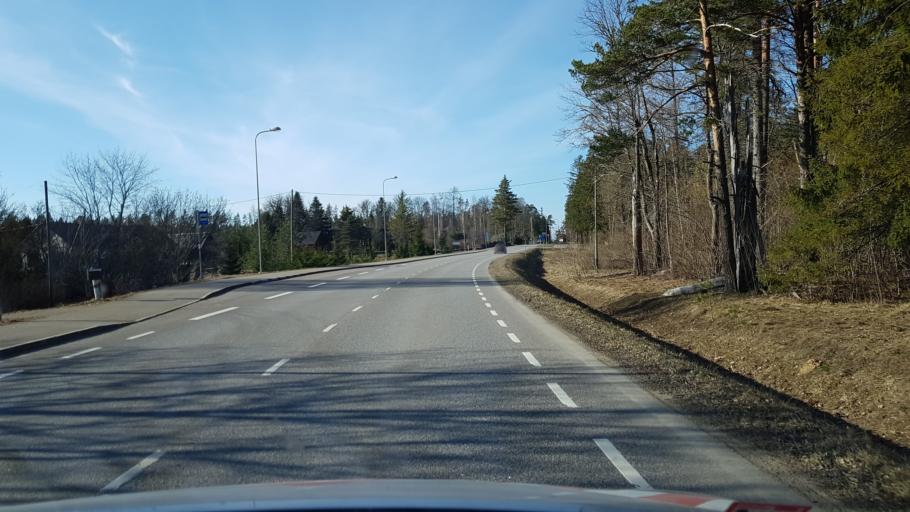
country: EE
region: Laeaene-Virumaa
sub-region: Vinni vald
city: Vinni
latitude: 59.1726
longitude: 26.5814
